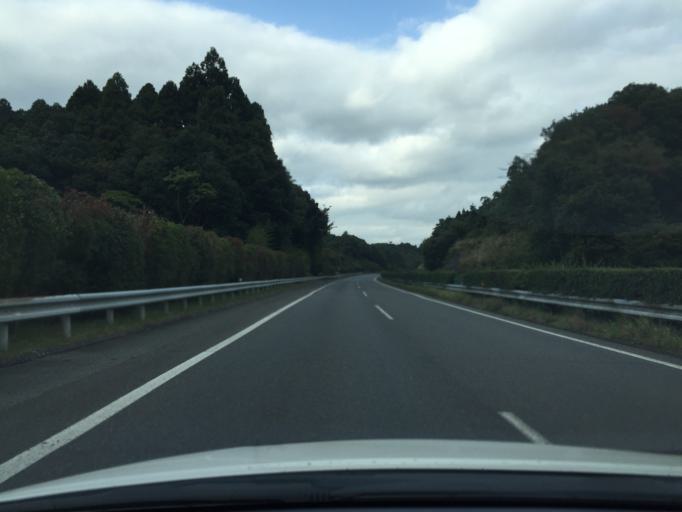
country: JP
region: Fukushima
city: Iwaki
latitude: 36.9420
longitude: 140.7720
